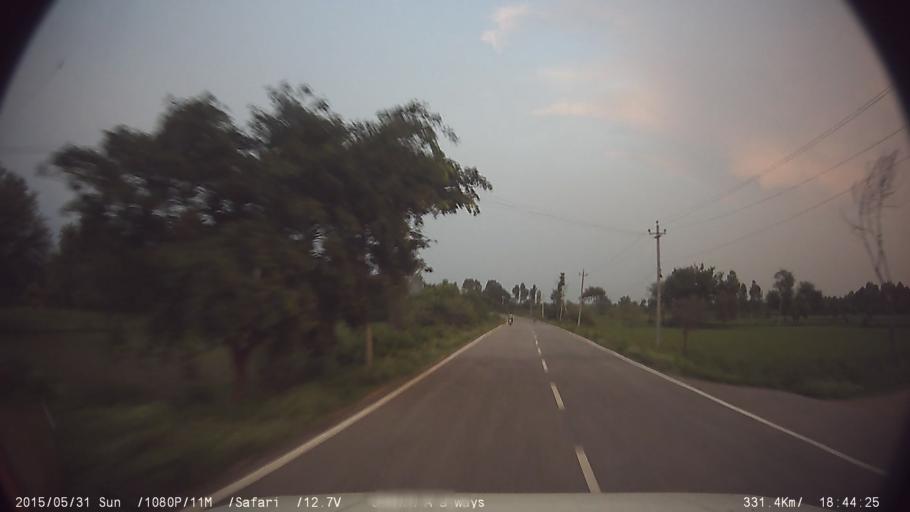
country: IN
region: Karnataka
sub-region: Mysore
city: Tirumakudal Narsipur
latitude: 12.1570
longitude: 76.8153
